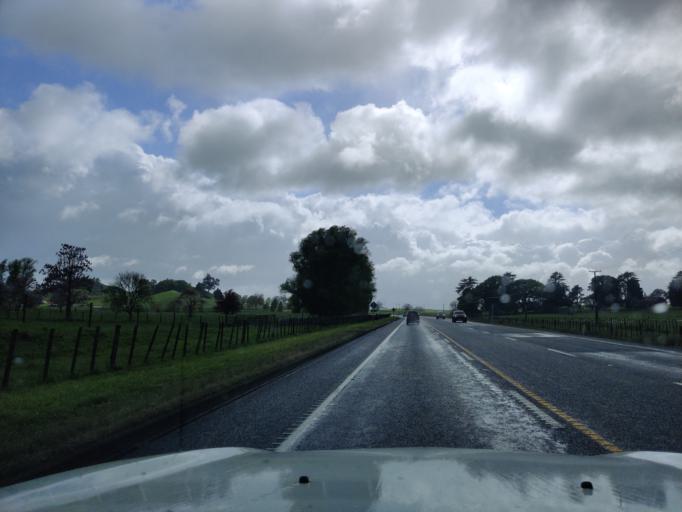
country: NZ
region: Waikato
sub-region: Matamata-Piako District
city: Matamata
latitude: -37.9845
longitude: 175.7316
